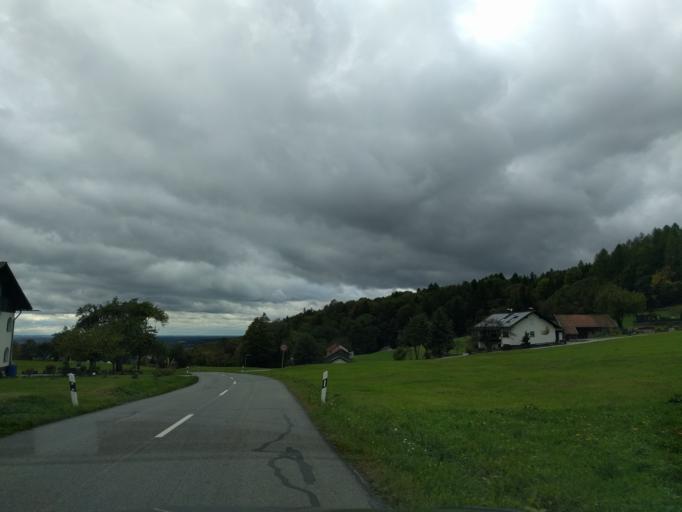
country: DE
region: Bavaria
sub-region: Lower Bavaria
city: Deggendorf
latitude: 48.8347
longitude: 12.9877
